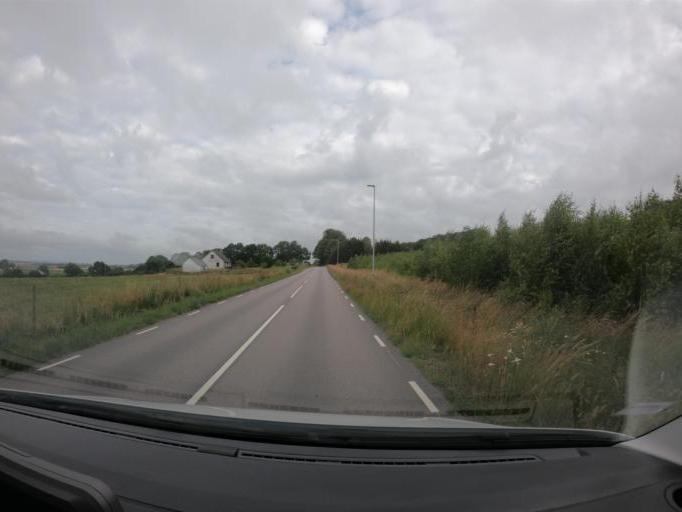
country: SE
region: Skane
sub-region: Bastads Kommun
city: Forslov
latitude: 56.3308
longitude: 12.9008
